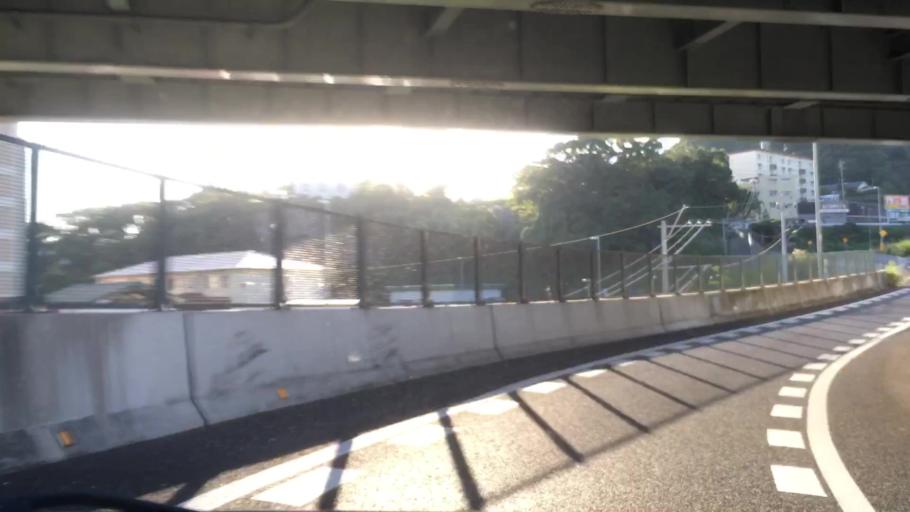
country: JP
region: Nagasaki
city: Sasebo
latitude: 33.1725
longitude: 129.7125
